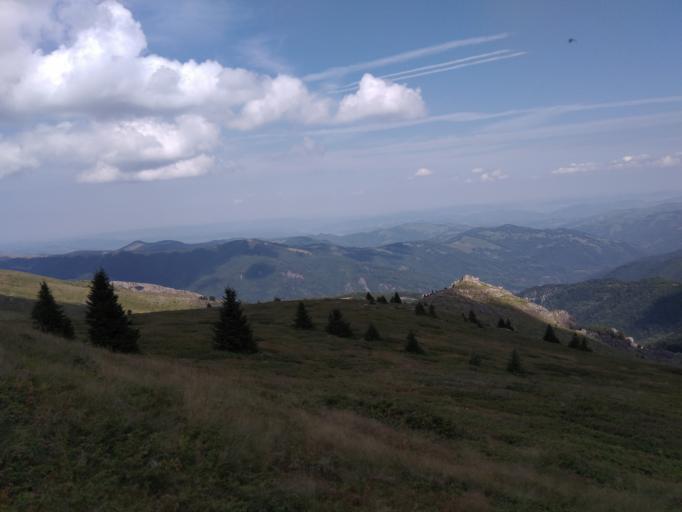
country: BG
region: Plovdiv
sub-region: Obshtina Karlovo
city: Karlovo
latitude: 42.7347
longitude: 24.7320
